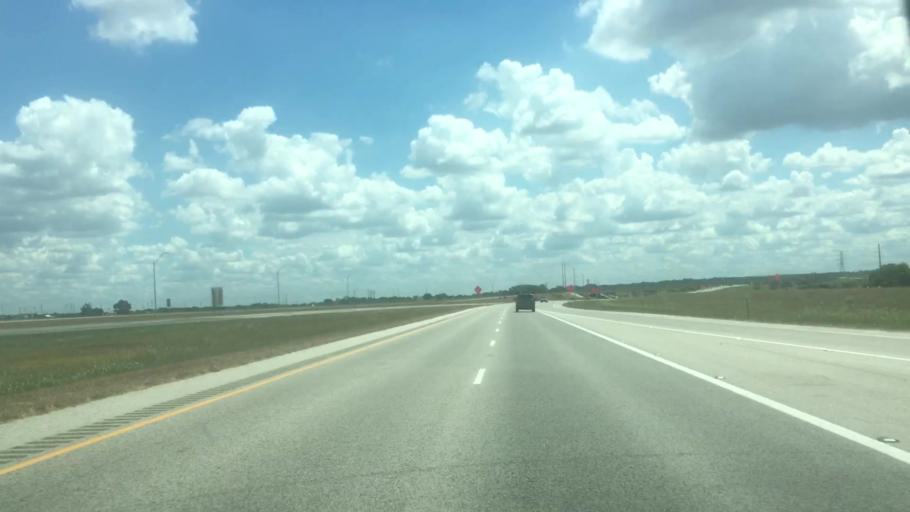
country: US
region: Texas
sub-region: Caldwell County
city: Lockhart
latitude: 29.8756
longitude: -97.7095
